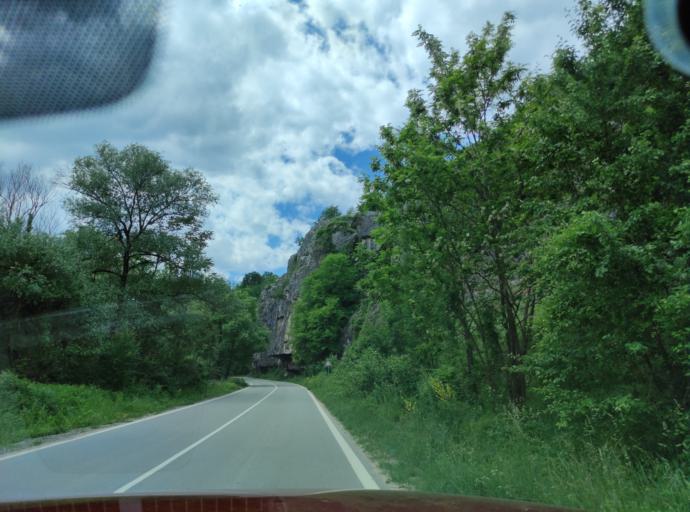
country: BG
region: Montana
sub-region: Obshtina Chiprovtsi
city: Chiprovtsi
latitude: 43.4422
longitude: 22.9343
